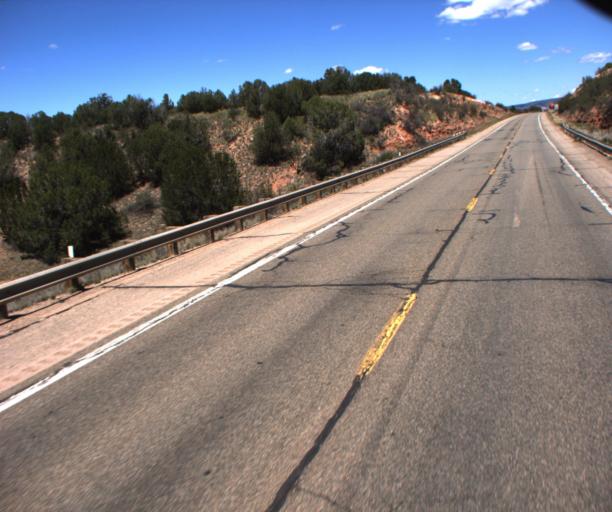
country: US
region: Arizona
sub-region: Yavapai County
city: Paulden
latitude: 34.9795
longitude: -112.4019
